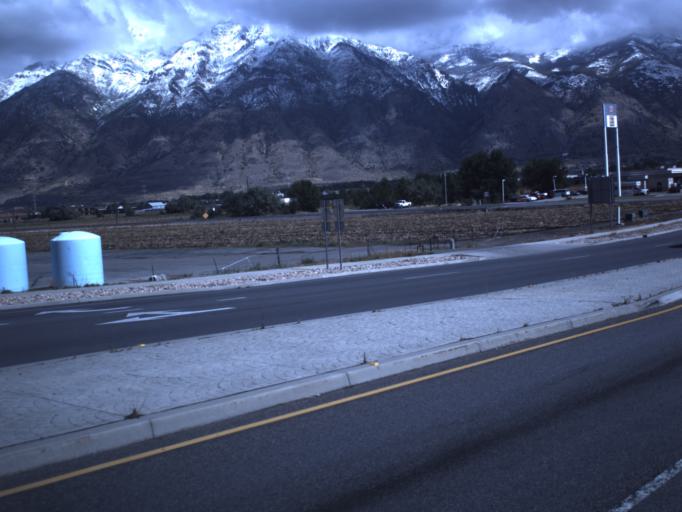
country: US
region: Utah
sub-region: Utah County
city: Springville
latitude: 40.1612
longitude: -111.6453
